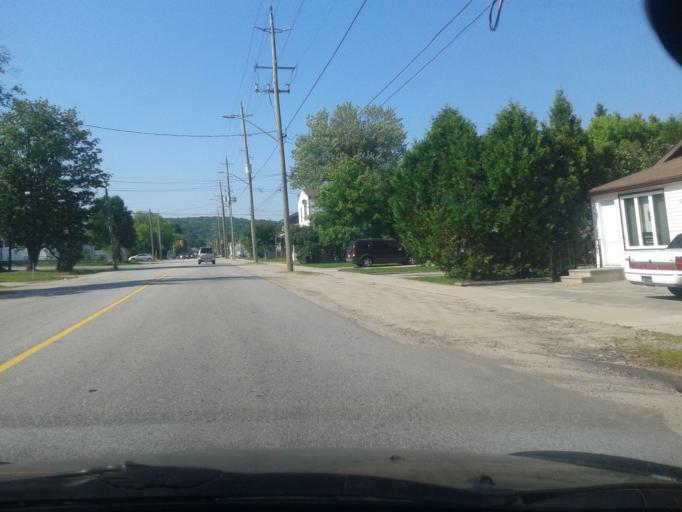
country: CA
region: Ontario
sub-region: Nipissing District
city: North Bay
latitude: 46.3257
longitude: -79.4572
